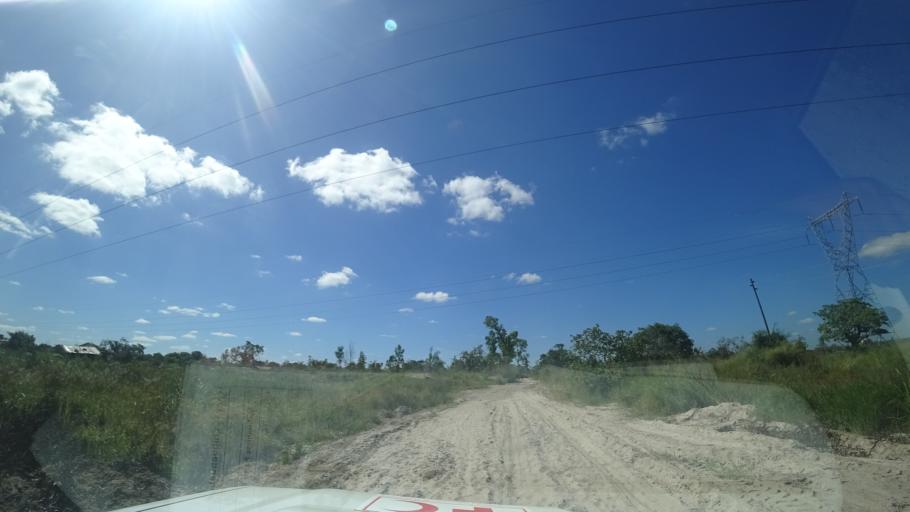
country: MZ
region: Sofala
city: Dondo
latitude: -19.5058
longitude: 34.6102
